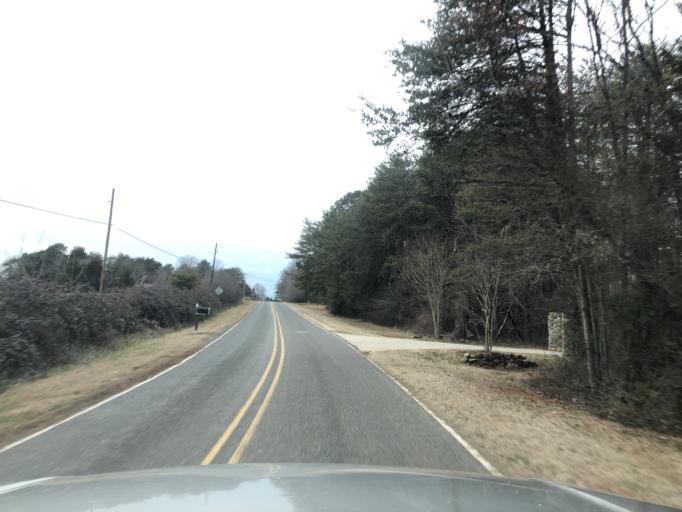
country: US
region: North Carolina
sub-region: Cleveland County
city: Shelby
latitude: 35.3380
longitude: -81.5359
